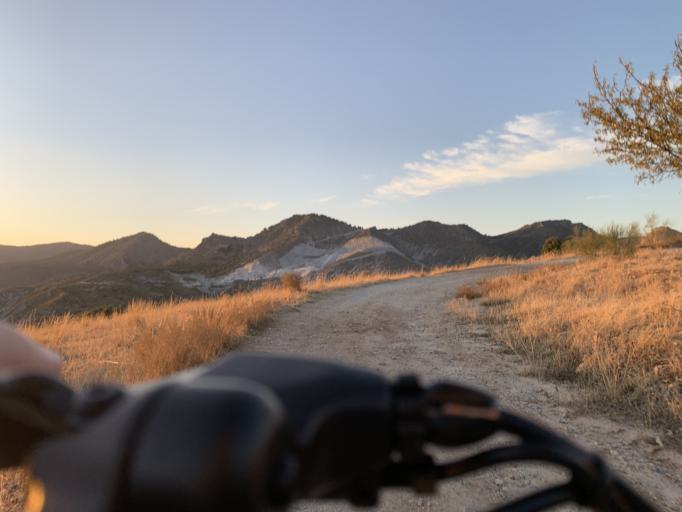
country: ES
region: Andalusia
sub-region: Provincia de Granada
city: Beas de Granada
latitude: 37.2248
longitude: -3.4680
